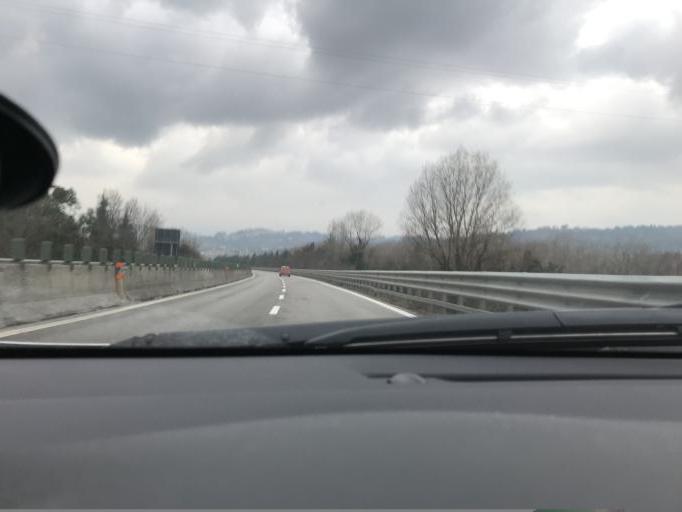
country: IT
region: The Marches
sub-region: Provincia di Ancona
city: Moie
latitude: 43.4951
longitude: 13.1184
